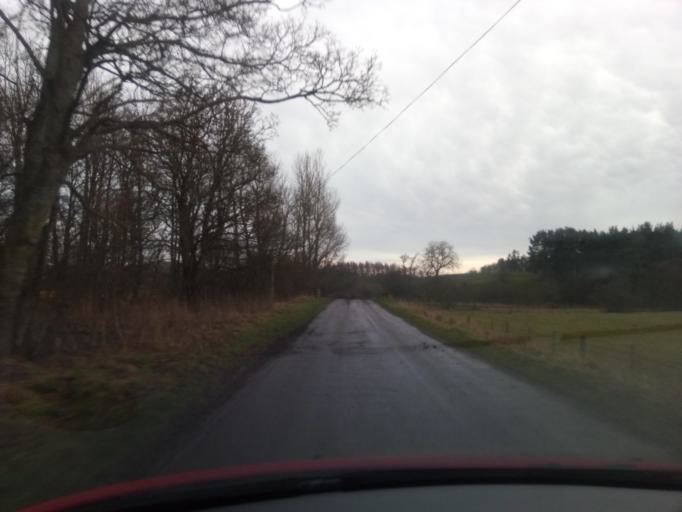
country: GB
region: England
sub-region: Northumberland
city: Wooler
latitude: 55.5055
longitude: -1.9277
